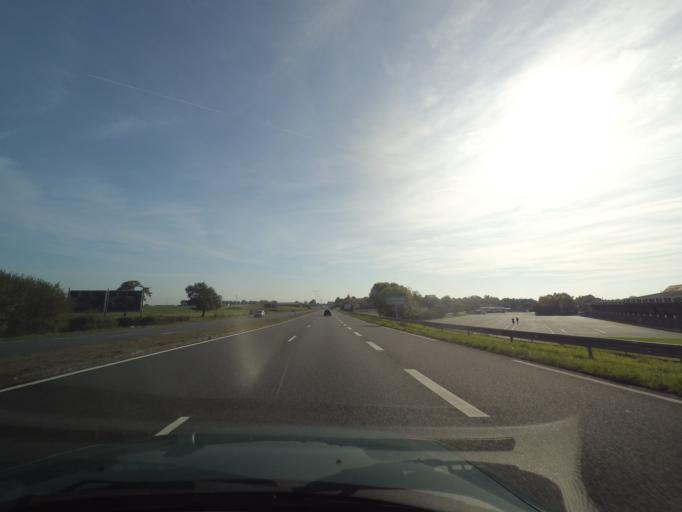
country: FR
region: Pays de la Loire
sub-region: Departement de Maine-et-Loire
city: Cholet
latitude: 47.0749
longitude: -0.8793
